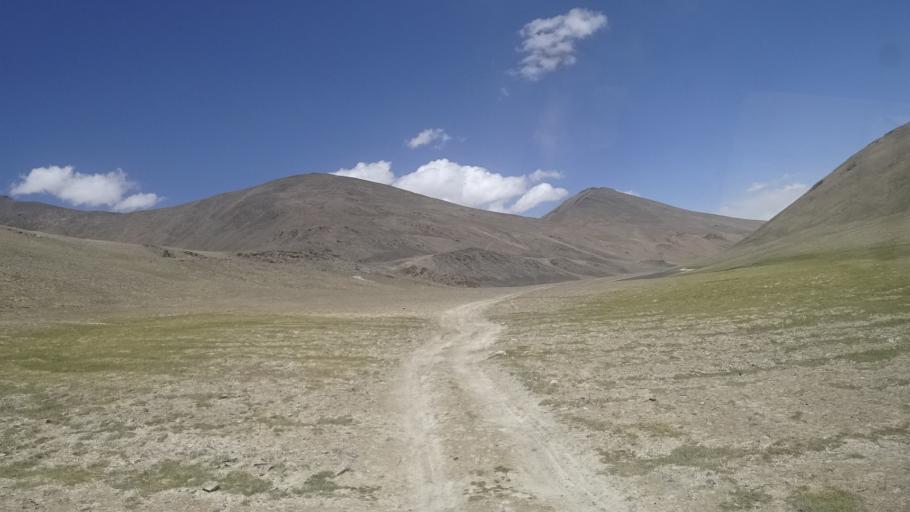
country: TJ
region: Gorno-Badakhshan
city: Murghob
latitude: 37.5179
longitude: 74.0584
